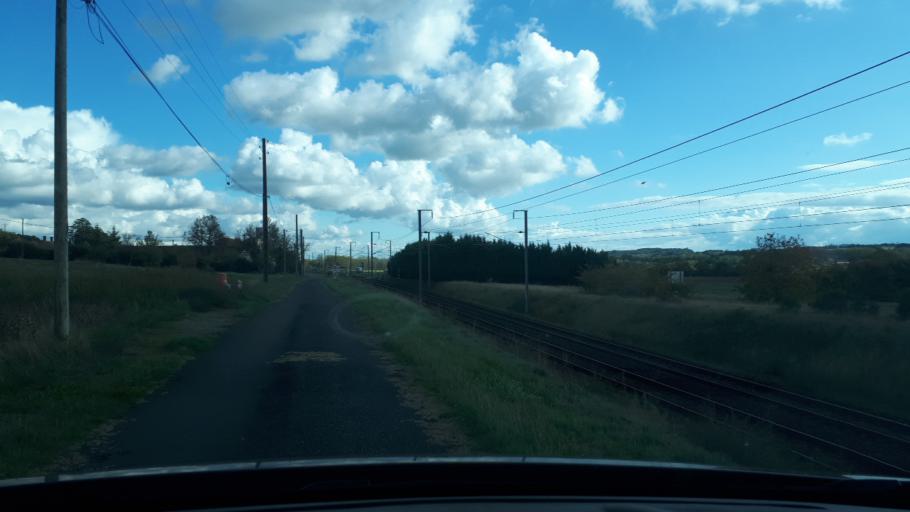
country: FR
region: Centre
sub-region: Departement du Loir-et-Cher
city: Mareuil-sur-Cher
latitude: 47.3021
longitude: 1.3523
